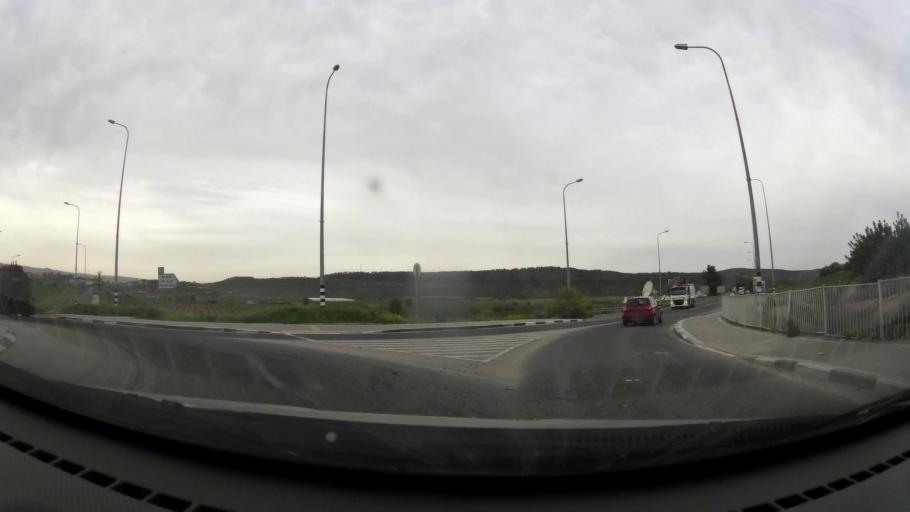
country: IL
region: Jerusalem
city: Bet Shemesh
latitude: 31.6818
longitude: 35.0023
